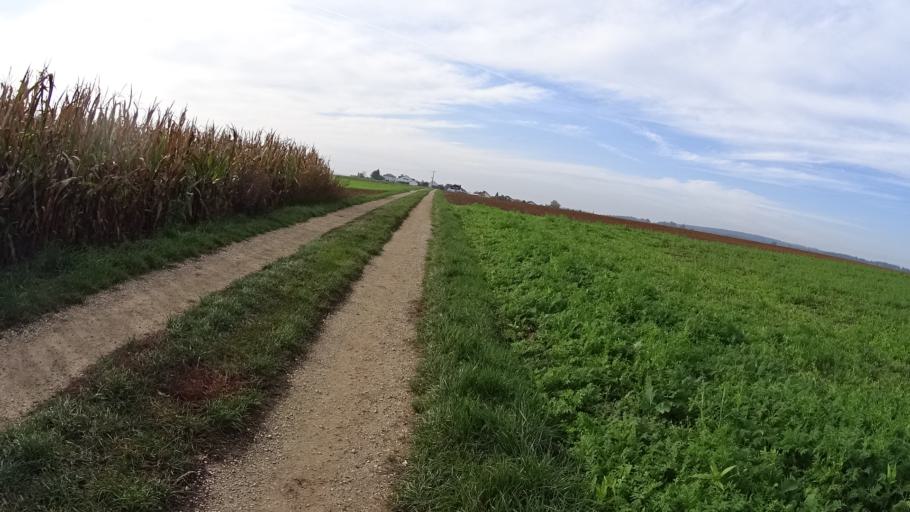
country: DE
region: Bavaria
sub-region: Upper Bavaria
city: Buxheim
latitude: 48.8206
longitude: 11.2891
